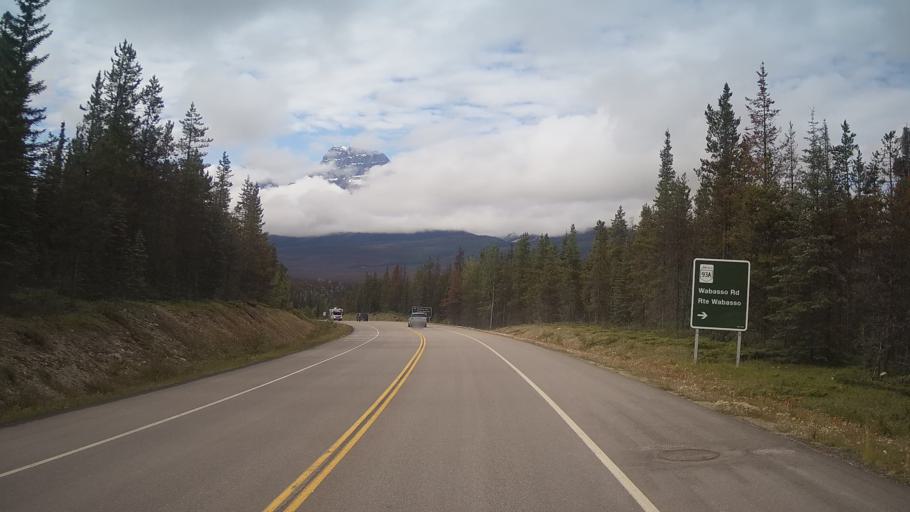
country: CA
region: Alberta
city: Jasper Park Lodge
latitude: 52.6749
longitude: -117.8801
